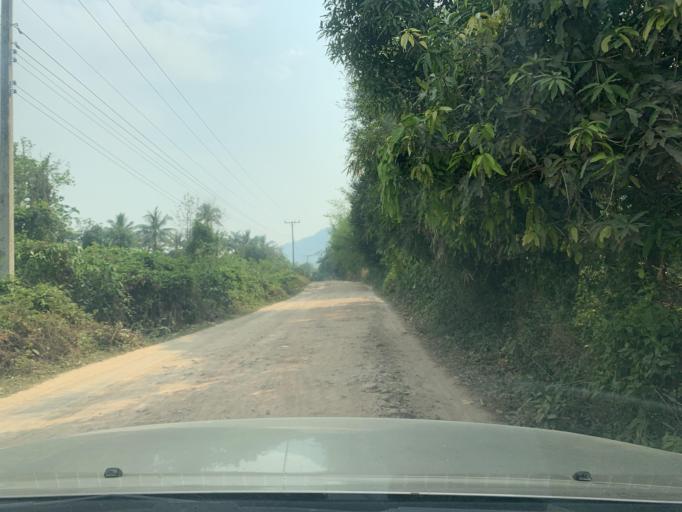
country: LA
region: Louangphabang
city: Louangphabang
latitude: 19.9098
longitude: 102.1342
